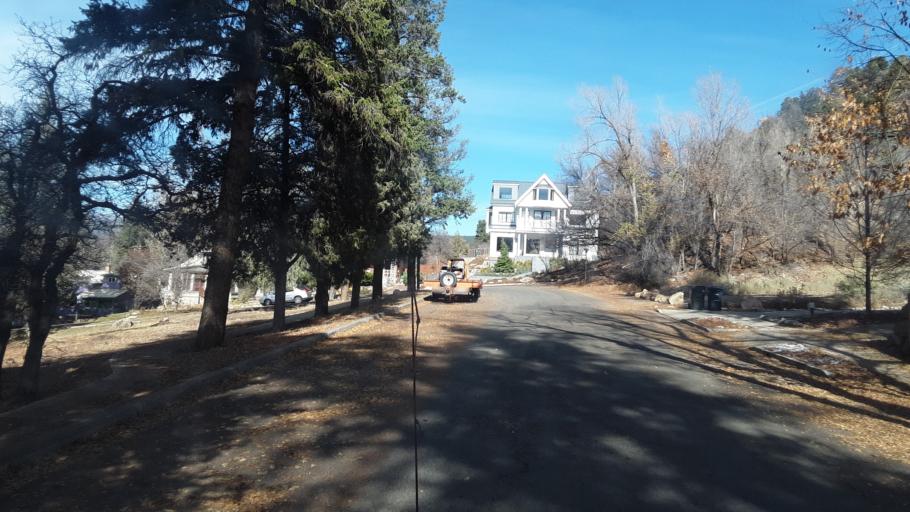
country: US
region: Colorado
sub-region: La Plata County
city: Durango
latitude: 37.2763
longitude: -107.8753
